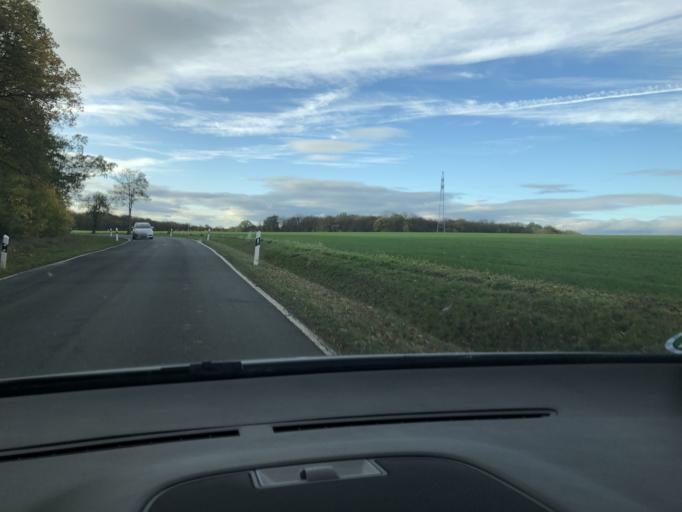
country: DE
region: Thuringia
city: Lehesten
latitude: 50.9708
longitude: 11.5931
